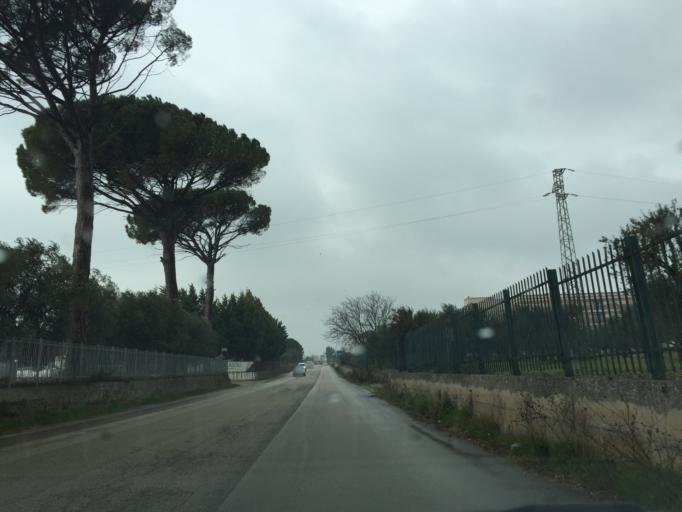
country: IT
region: Apulia
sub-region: Provincia di Foggia
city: Troia
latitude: 41.3689
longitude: 15.3369
